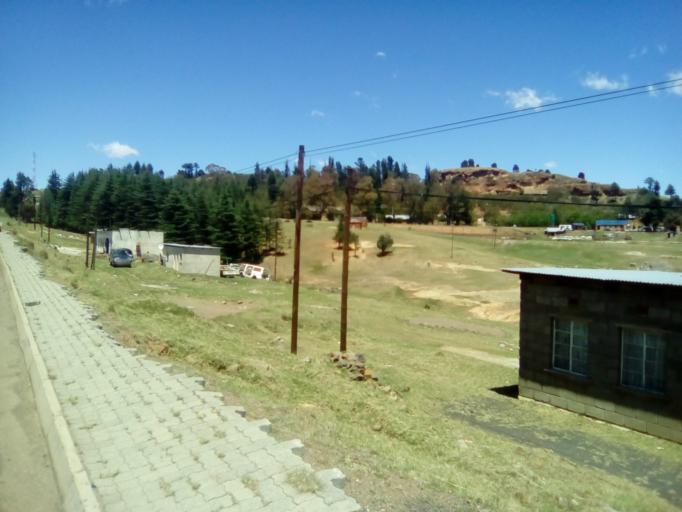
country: LS
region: Qacha's Nek
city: Qacha's Nek
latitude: -30.1185
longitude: 28.6915
